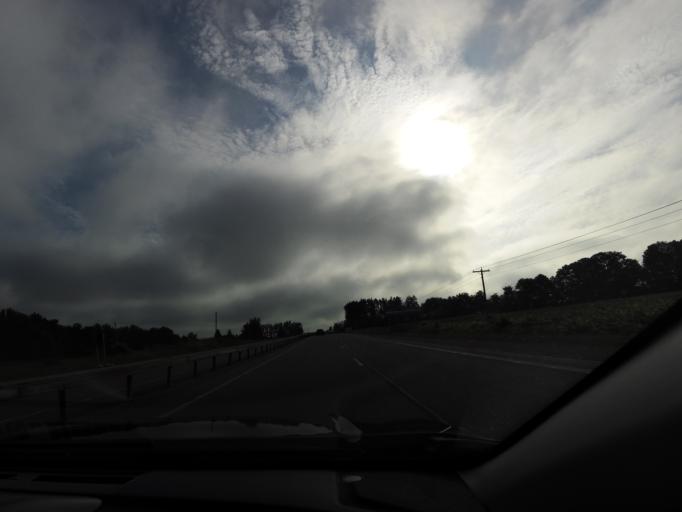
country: CA
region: Ontario
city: Barrie
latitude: 44.4499
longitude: -79.6028
